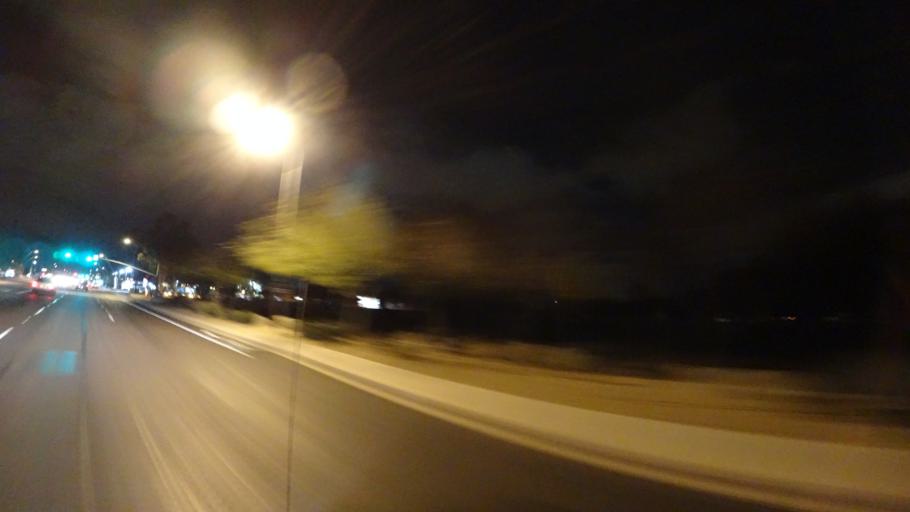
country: US
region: Arizona
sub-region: Maricopa County
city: San Carlos
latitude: 33.3320
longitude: -111.8591
